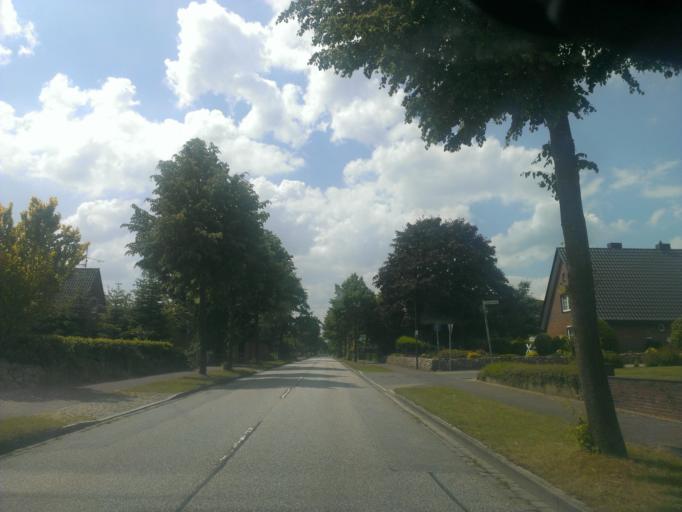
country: DE
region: Schleswig-Holstein
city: Fockbek
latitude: 54.3012
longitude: 9.5966
